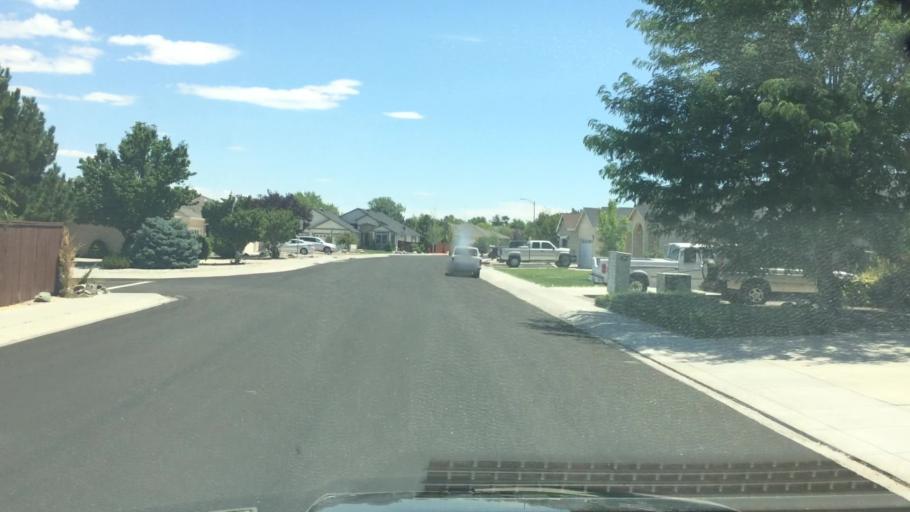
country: US
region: Nevada
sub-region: Lyon County
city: Fernley
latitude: 39.5839
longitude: -119.1427
